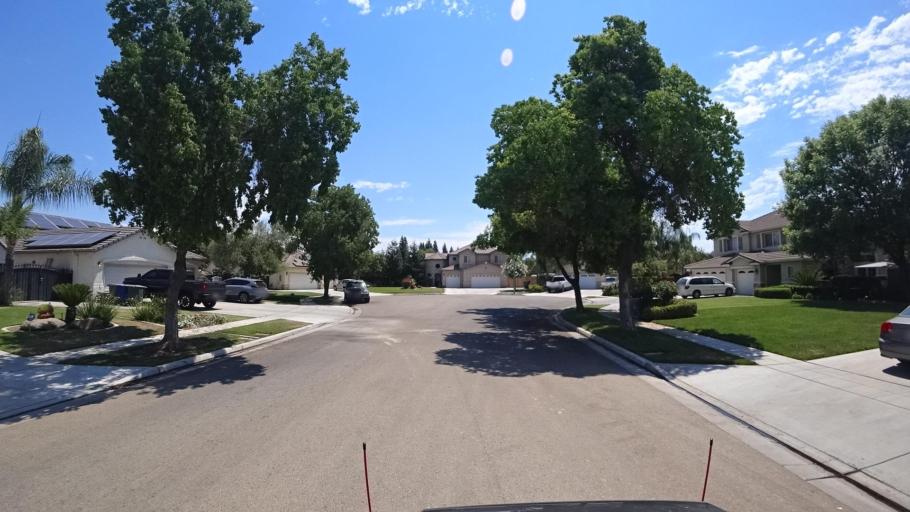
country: US
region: California
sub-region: Fresno County
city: Sunnyside
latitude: 36.7268
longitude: -119.7125
